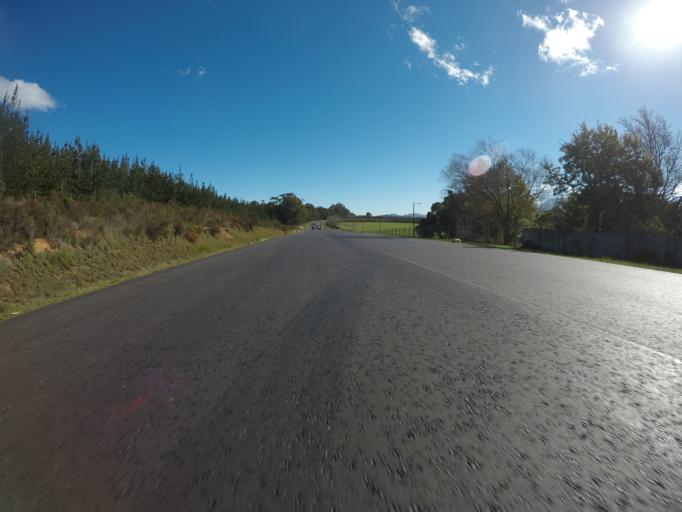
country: ZA
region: Western Cape
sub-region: Overberg District Municipality
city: Grabouw
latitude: -34.1780
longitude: 19.0676
